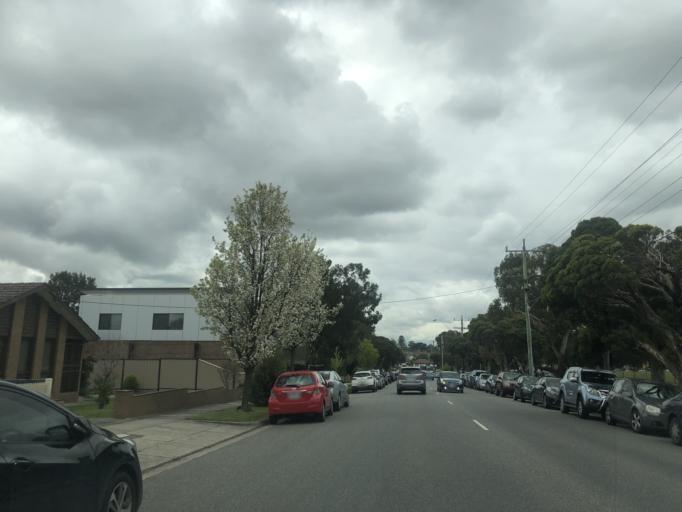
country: AU
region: Victoria
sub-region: Greater Dandenong
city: Dandenong North
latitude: -37.9732
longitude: 145.2167
